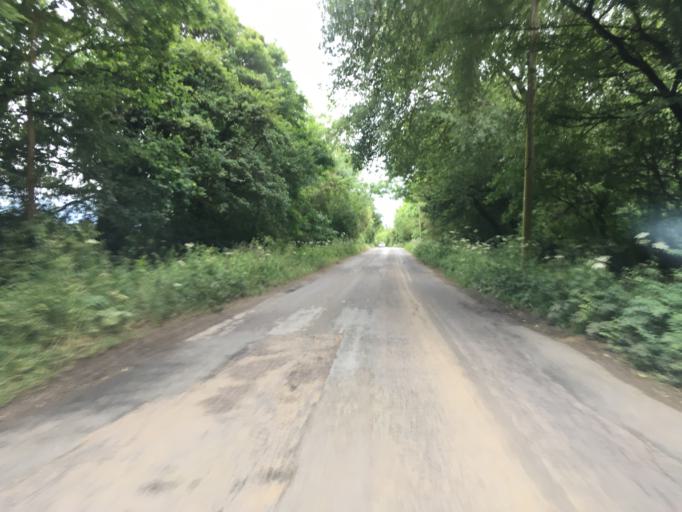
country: GB
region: England
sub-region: Wiltshire
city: Norton
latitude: 51.5910
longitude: -2.1780
